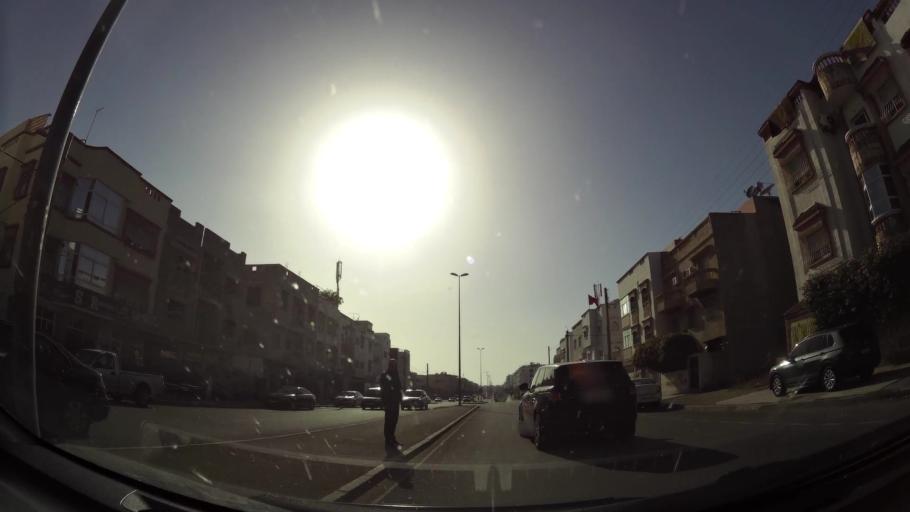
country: MA
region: Oued ed Dahab-Lagouira
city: Dakhla
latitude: 30.3948
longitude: -9.5363
